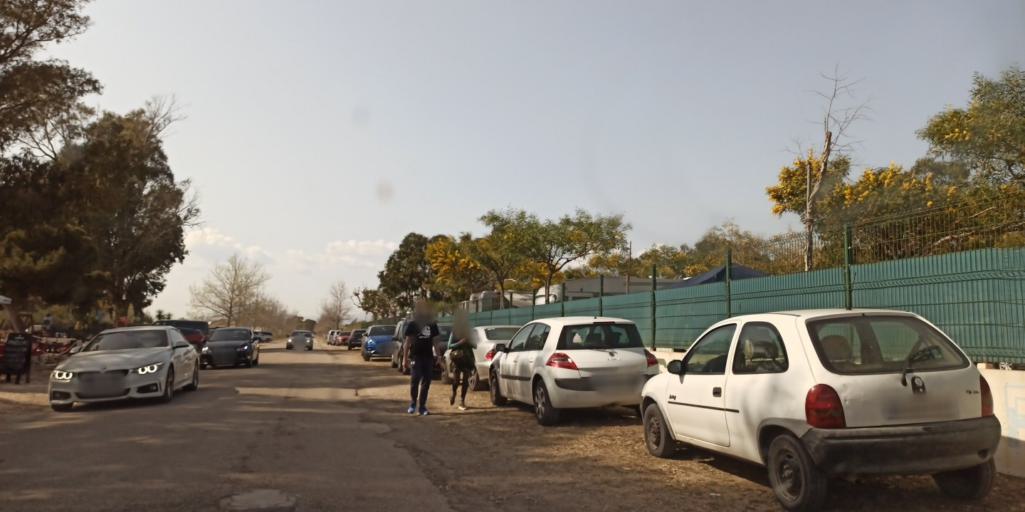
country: ES
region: Catalonia
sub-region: Provincia de Tarragona
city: Deltebre
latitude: 40.7205
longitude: 0.8479
